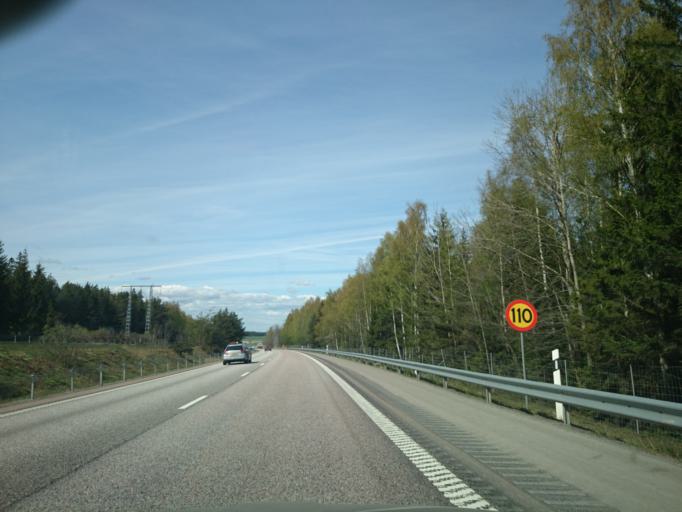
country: SE
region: Uppsala
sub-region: Uppsala Kommun
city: Alsike
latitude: 59.7999
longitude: 17.7695
